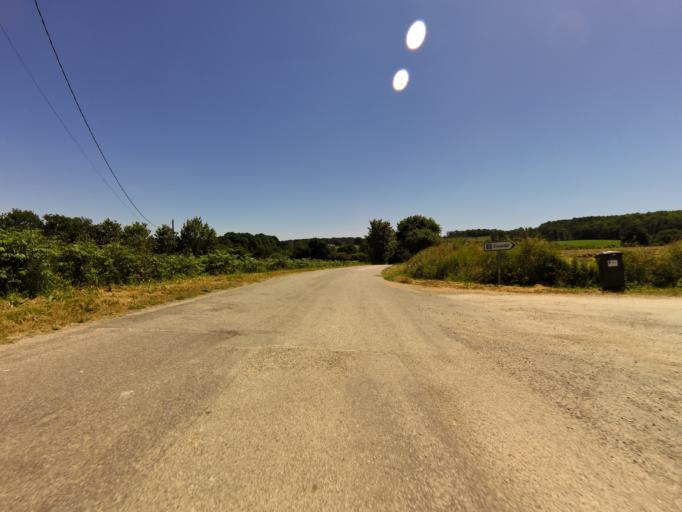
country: FR
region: Brittany
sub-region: Departement du Morbihan
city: Molac
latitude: 47.7111
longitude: -2.4070
